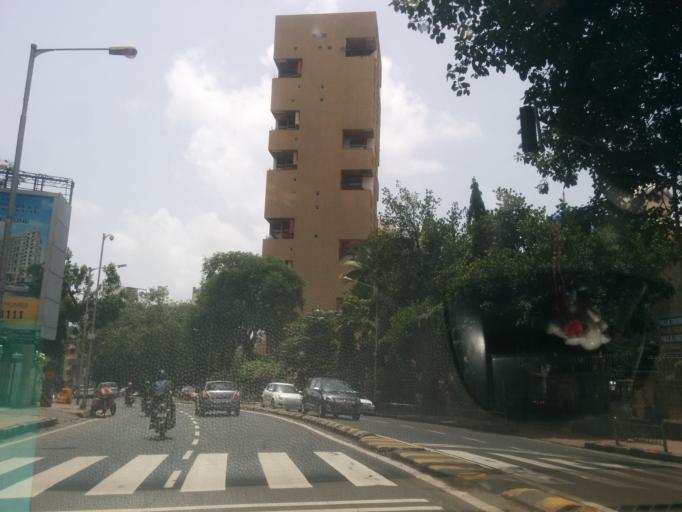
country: IN
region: Maharashtra
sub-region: Mumbai Suburban
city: Mumbai
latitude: 18.9664
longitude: 72.8076
